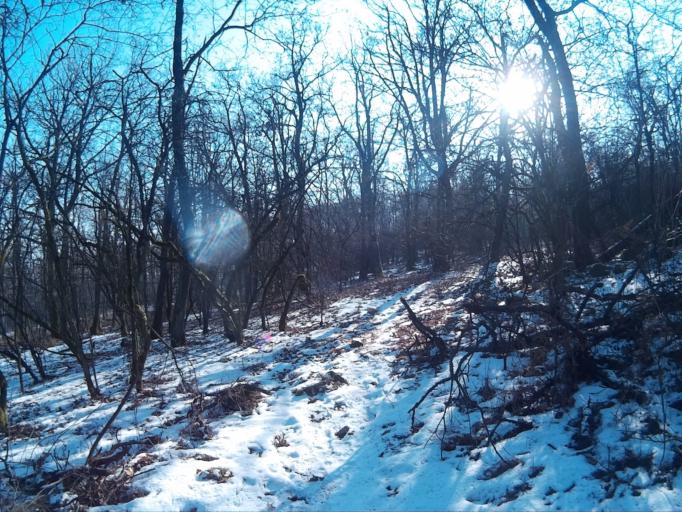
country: HU
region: Nograd
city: Paszto
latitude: 47.9646
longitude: 19.6459
